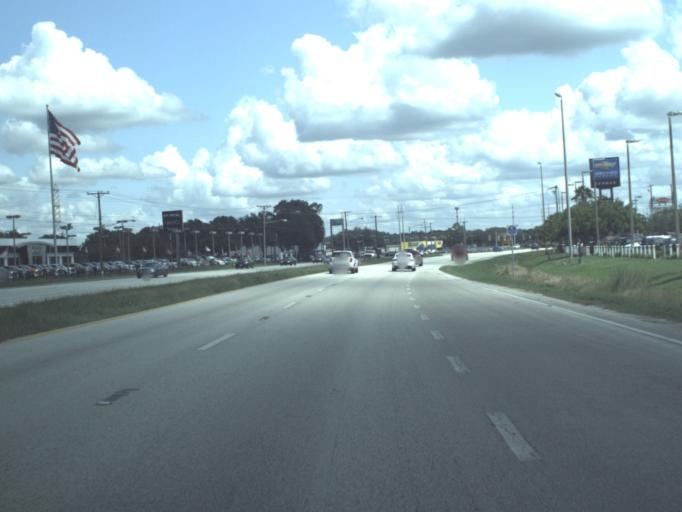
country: US
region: Florida
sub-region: Hillsborough County
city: Palm River-Clair Mel
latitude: 27.9495
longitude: -82.3469
